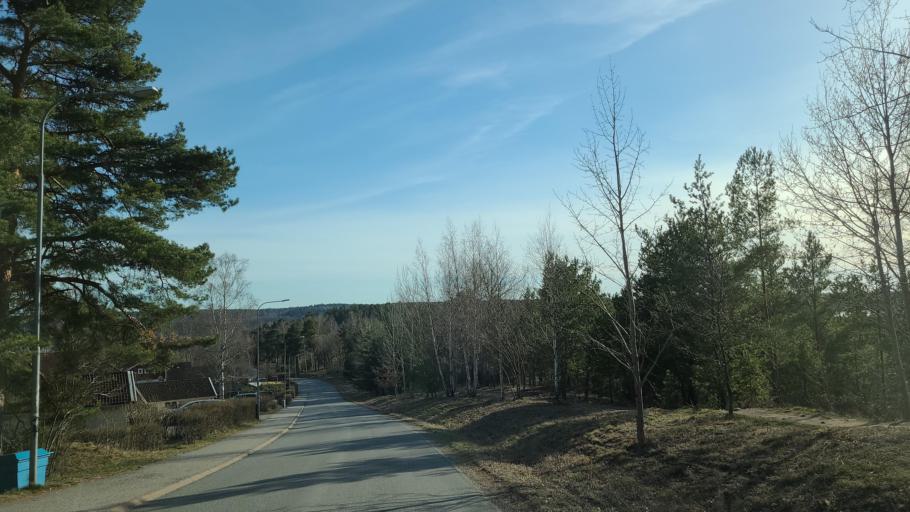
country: SE
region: Stockholm
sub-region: Ekero Kommun
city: Ekeroe
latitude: 59.2726
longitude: 17.7833
